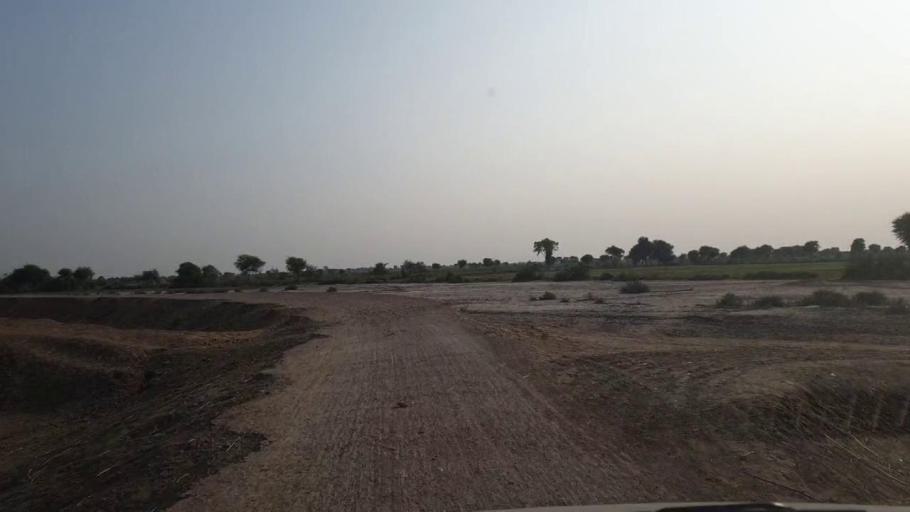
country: PK
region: Sindh
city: Rajo Khanani
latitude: 25.0240
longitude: 68.7804
